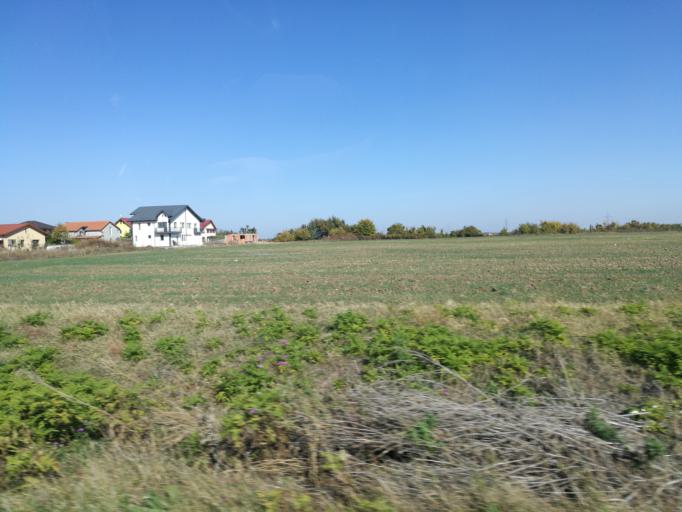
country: RO
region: Giurgiu
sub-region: Comuna Joita
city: Bacu
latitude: 44.4745
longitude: 25.9095
